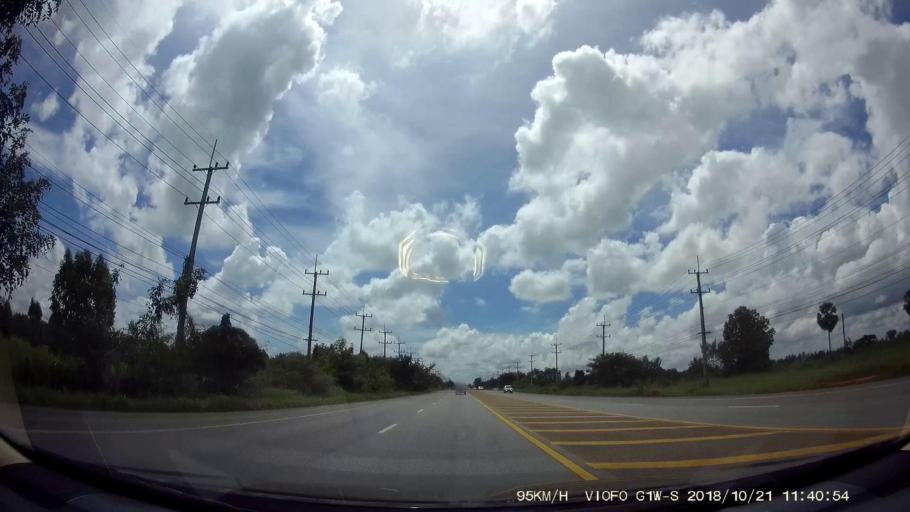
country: TH
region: Chaiyaphum
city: Chaiyaphum
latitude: 15.7071
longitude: 102.0152
